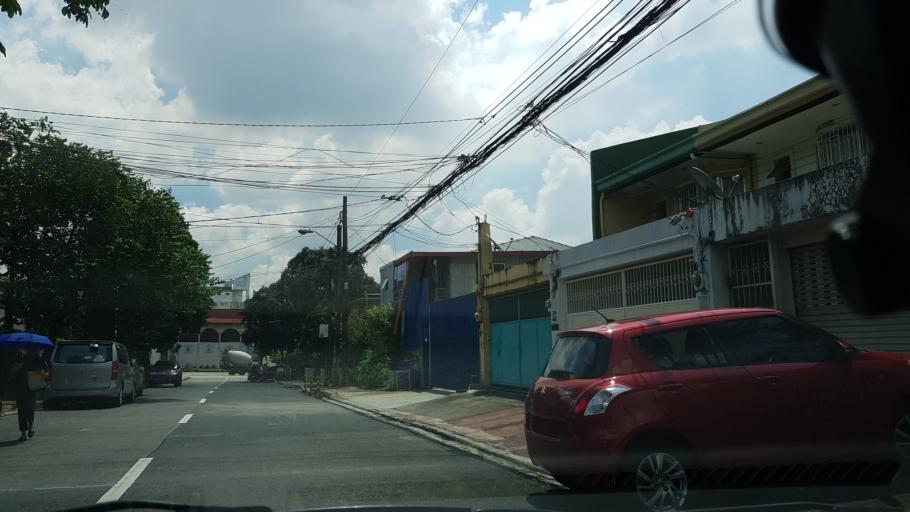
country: PH
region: Metro Manila
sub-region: Quezon City
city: Quezon City
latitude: 14.6305
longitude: 121.0399
